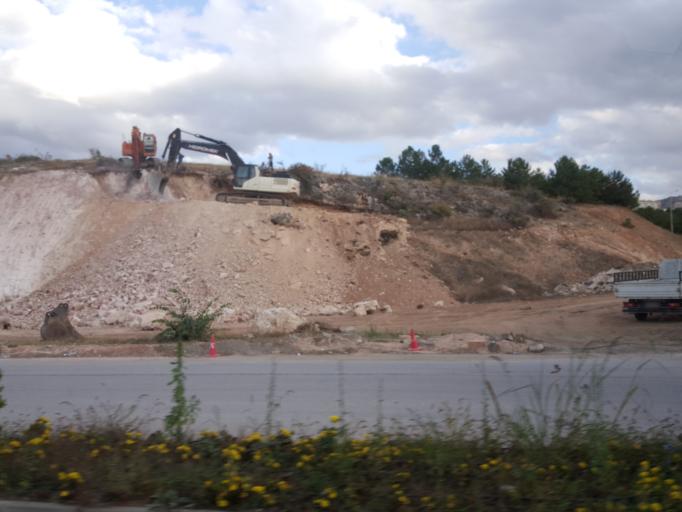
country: TR
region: Tokat
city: Tokat
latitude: 40.3337
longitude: 36.4813
